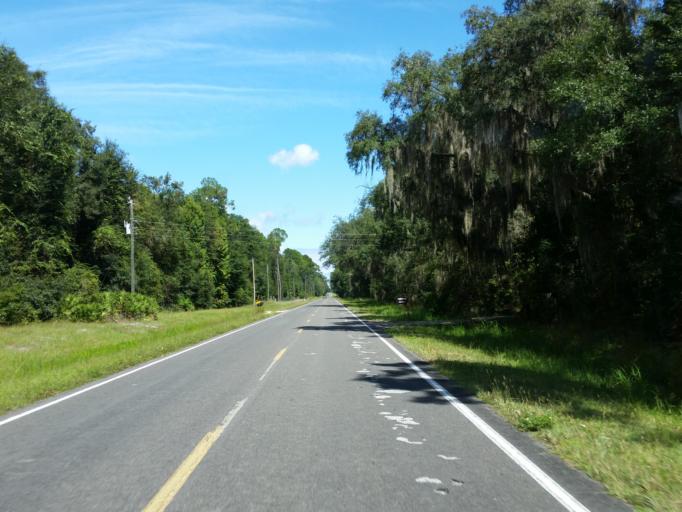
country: US
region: Florida
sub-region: Alachua County
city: Gainesville
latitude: 29.5785
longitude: -82.2471
